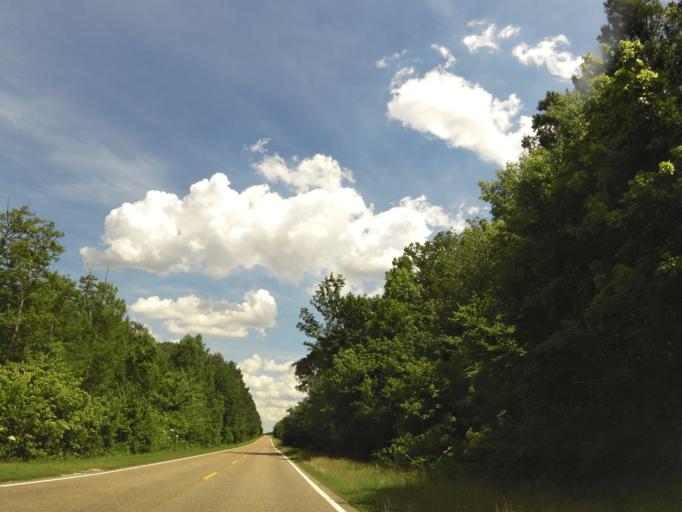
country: US
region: Tennessee
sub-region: Dyer County
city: Newbern
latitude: 36.0208
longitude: -89.1694
